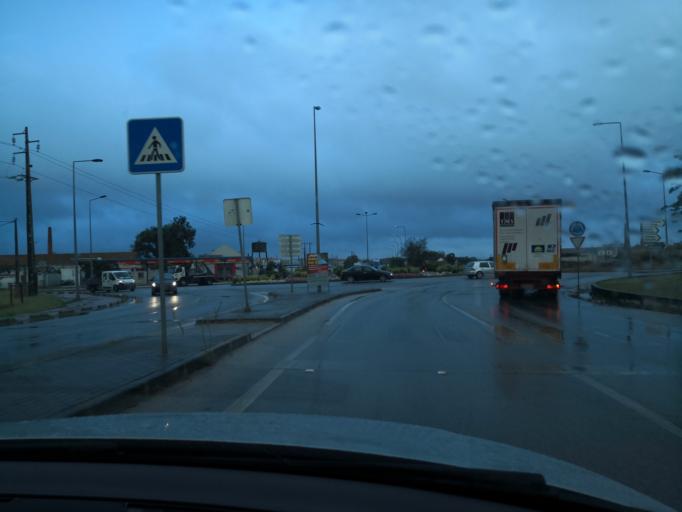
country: PT
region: Setubal
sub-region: Moita
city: Moita
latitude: 38.6494
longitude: -8.9975
